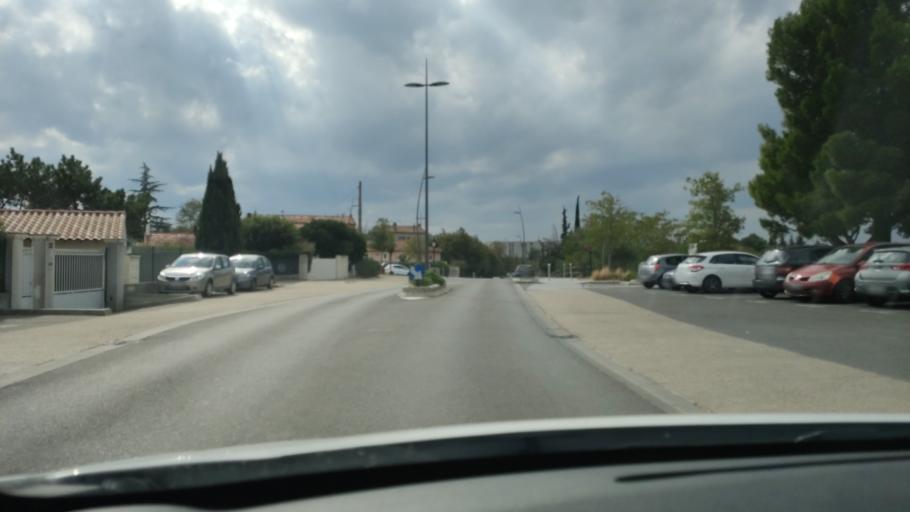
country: FR
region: Languedoc-Roussillon
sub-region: Departement du Gard
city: Les Angles
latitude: 43.9616
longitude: 4.7700
